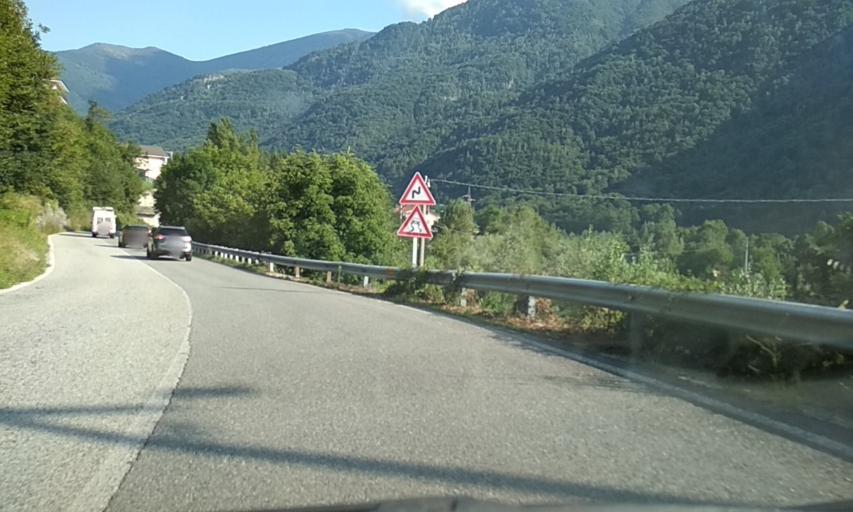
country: IT
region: Piedmont
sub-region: Provincia di Torino
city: Locana
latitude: 45.4115
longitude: 7.4801
